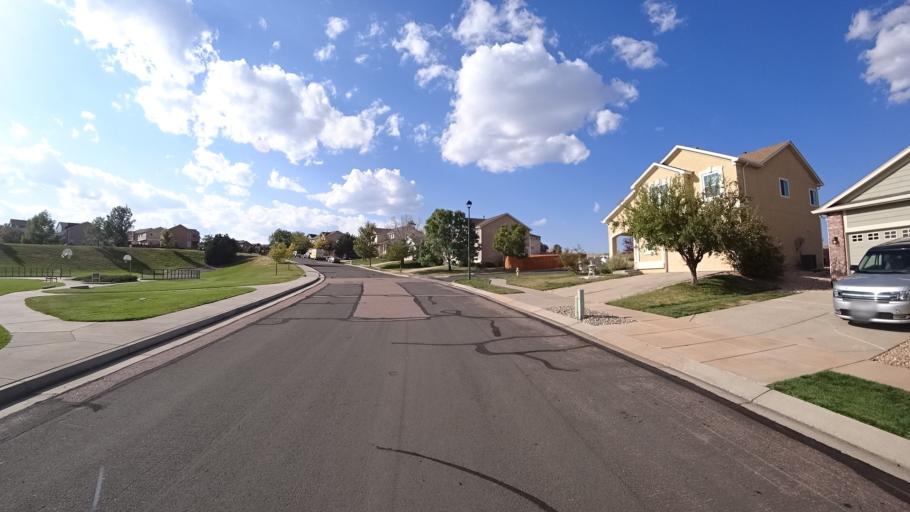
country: US
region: Colorado
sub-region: El Paso County
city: Cimarron Hills
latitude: 38.9113
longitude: -104.7241
